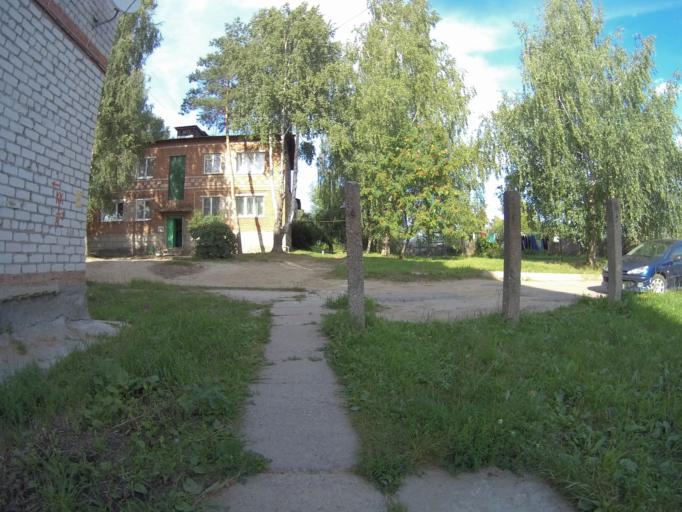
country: RU
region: Vladimir
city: Raduzhnyy
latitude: 56.0928
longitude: 40.2457
